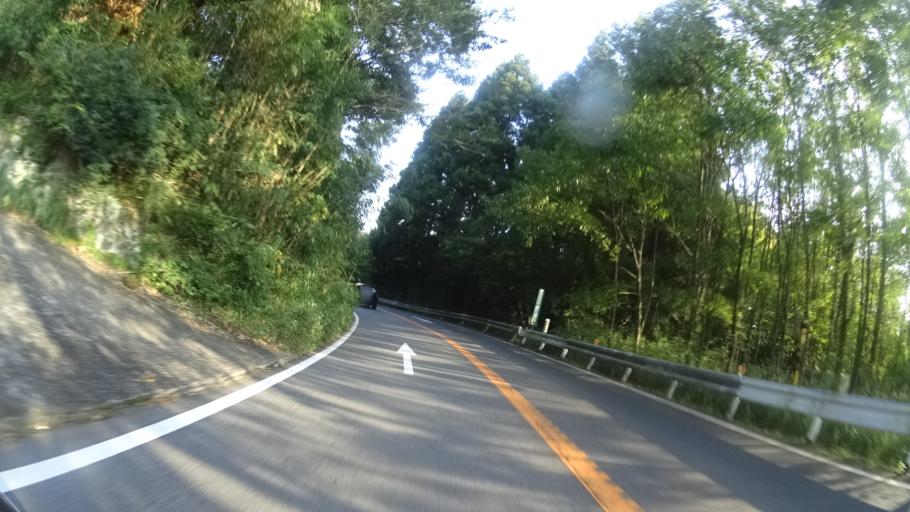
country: JP
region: Oita
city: Beppu
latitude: 33.2694
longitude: 131.4360
